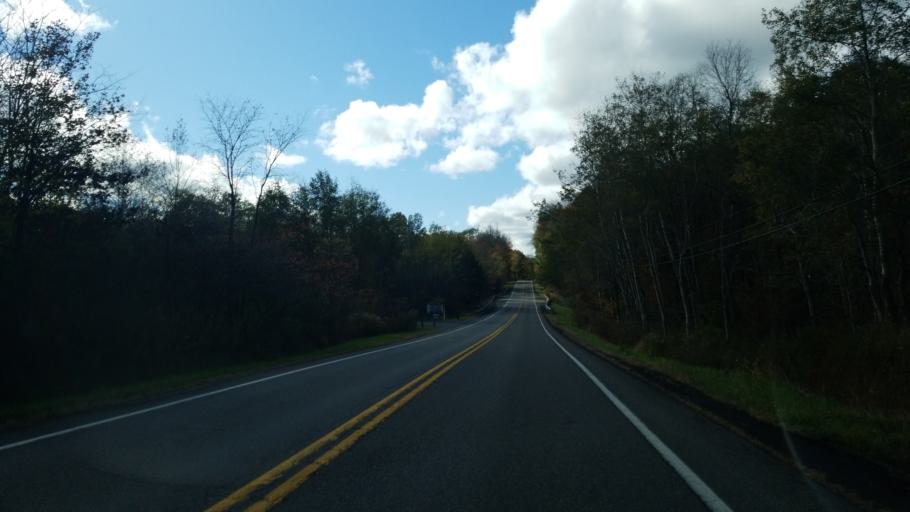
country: US
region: Pennsylvania
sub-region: Jefferson County
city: Sykesville
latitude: 41.0920
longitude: -78.8263
